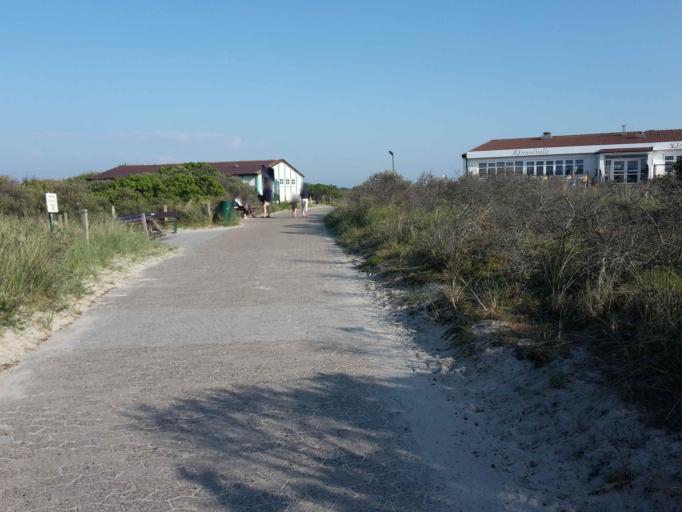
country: DE
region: Lower Saxony
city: Spiekeroog
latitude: 53.7788
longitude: 7.6963
